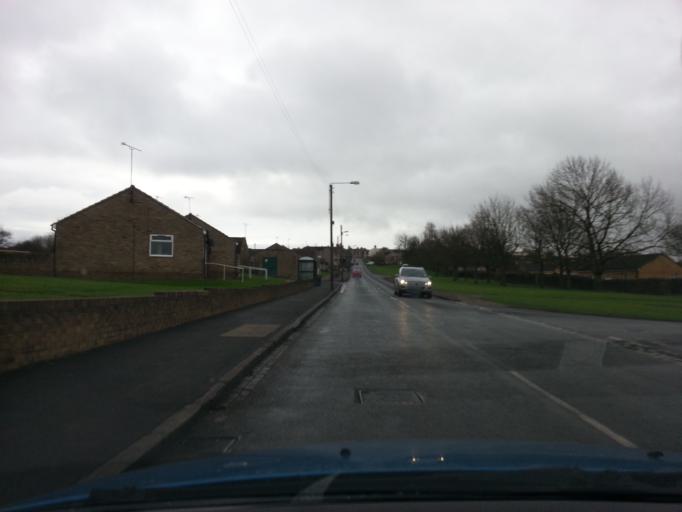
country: GB
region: England
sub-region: County Durham
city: Crook
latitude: 54.7127
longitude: -1.7368
